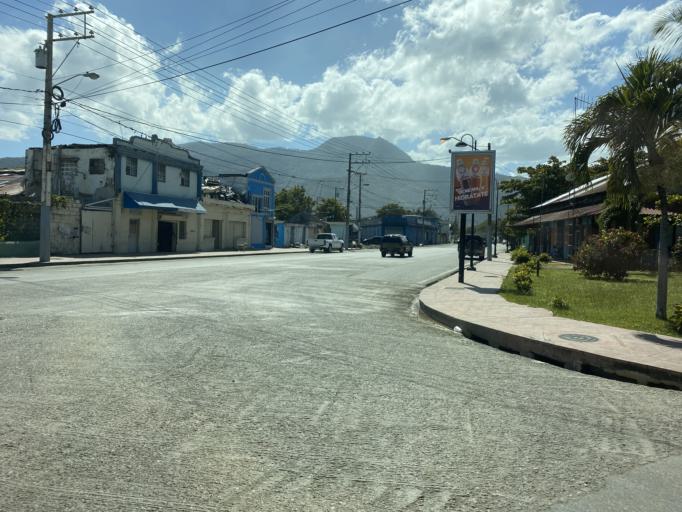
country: DO
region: Puerto Plata
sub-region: Puerto Plata
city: Puerto Plata
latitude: 19.7993
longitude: -70.6963
